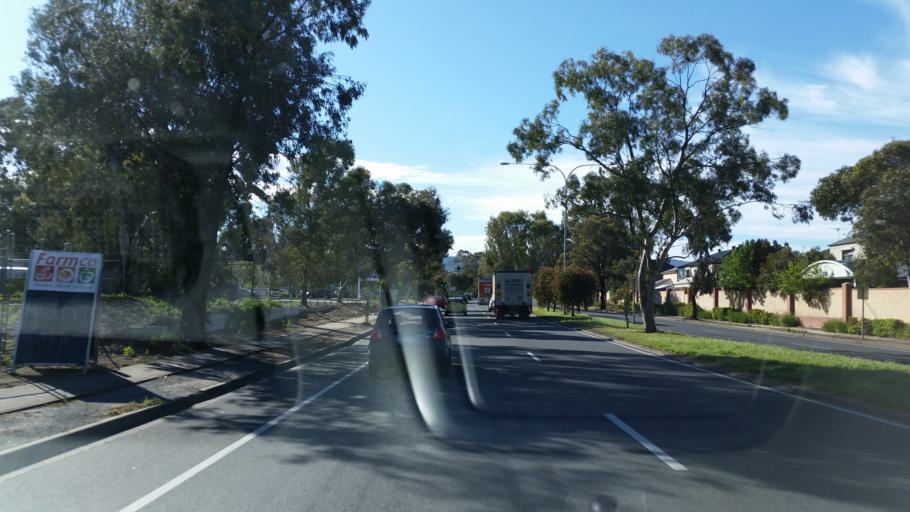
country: AU
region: South Australia
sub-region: Norwood Payneham St Peters
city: Marden
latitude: -34.8912
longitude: 138.6322
